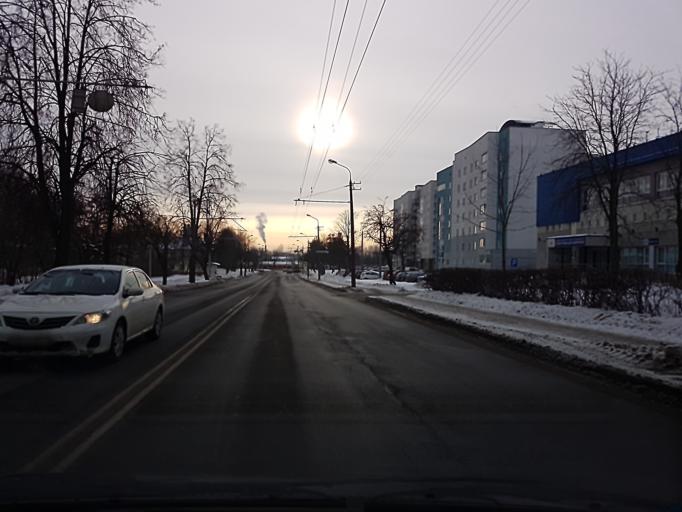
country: BY
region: Minsk
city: Minsk
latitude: 53.8830
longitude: 27.5188
